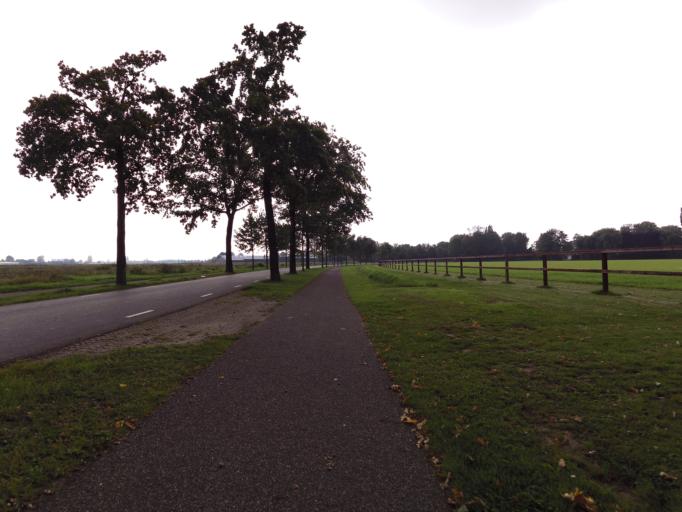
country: NL
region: Gelderland
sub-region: Gemeente Duiven
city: Duiven
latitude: 51.9380
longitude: 6.0008
